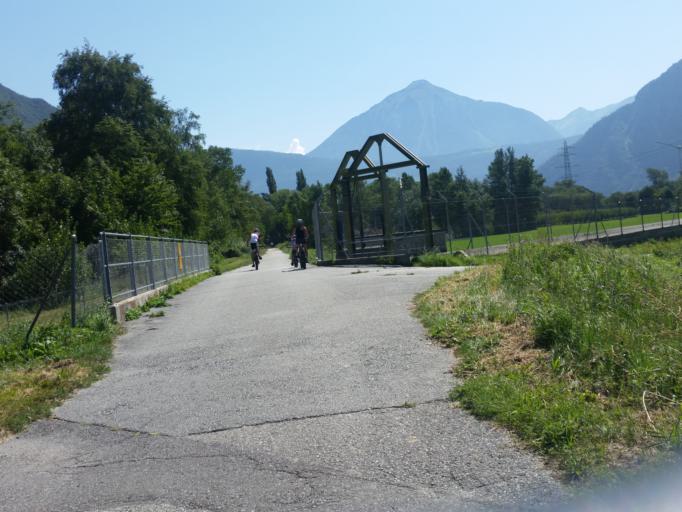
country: CH
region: Valais
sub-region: Saint-Maurice District
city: Vernayaz
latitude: 46.1390
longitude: 7.0494
